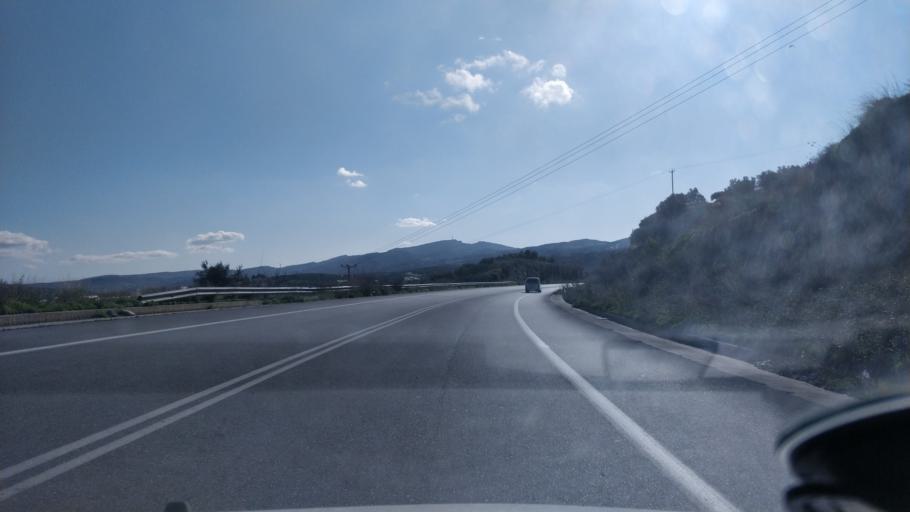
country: GR
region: Crete
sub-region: Nomos Irakleiou
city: Ano Arhanes
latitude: 35.2399
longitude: 25.1815
